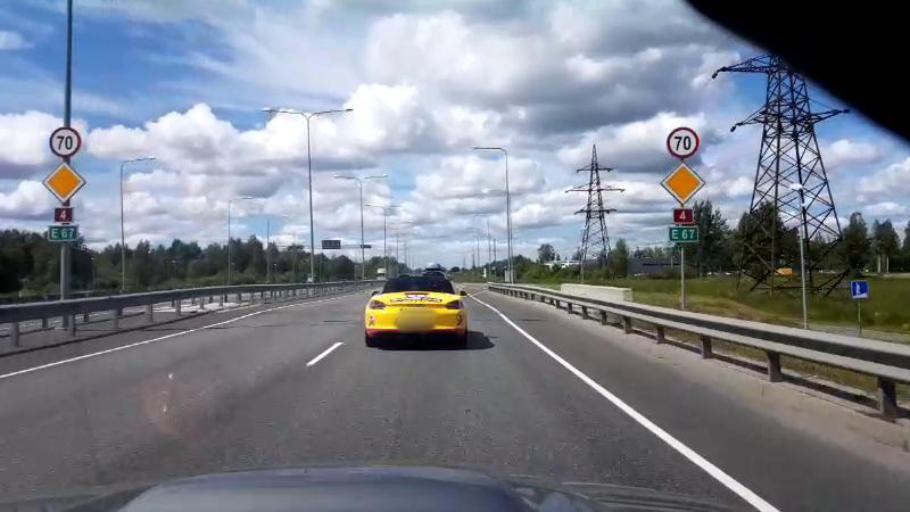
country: EE
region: Paernumaa
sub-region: Paernu linn
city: Parnu
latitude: 58.3937
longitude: 24.5346
